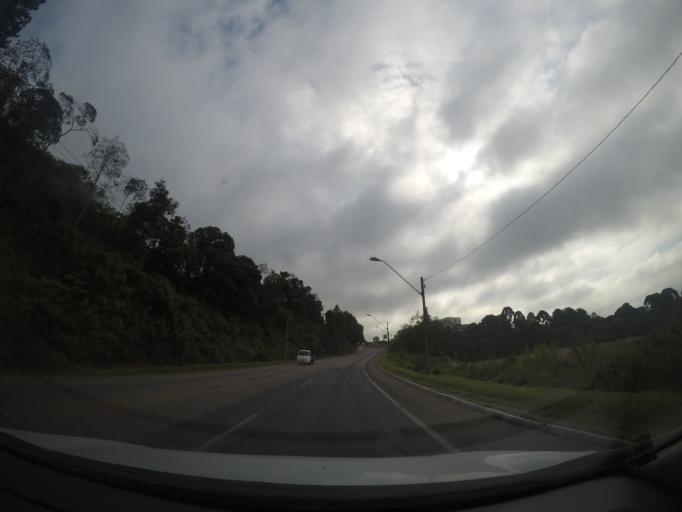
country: BR
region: Parana
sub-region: Colombo
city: Colombo
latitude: -25.3627
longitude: -49.2198
